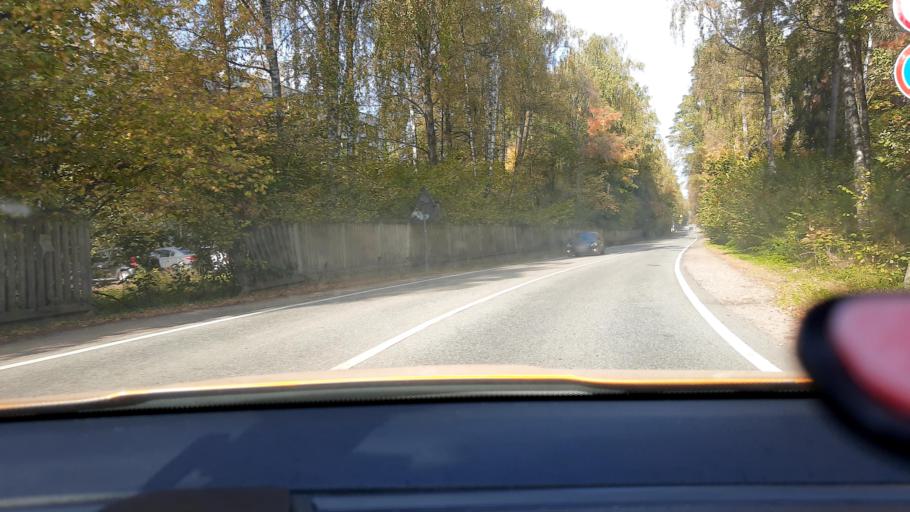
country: RU
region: Moskovskaya
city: Petrovo-Dal'neye
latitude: 55.7873
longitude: 37.2101
